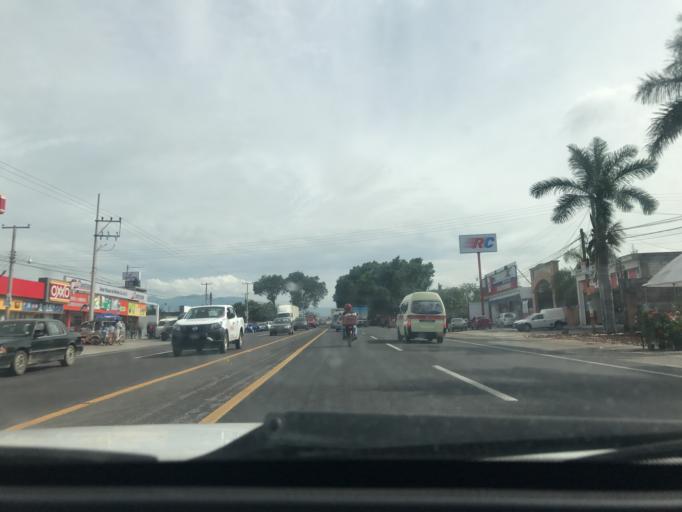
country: MX
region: Morelos
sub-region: Atlatlahucan
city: Colonia San Francisco
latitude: 18.8813
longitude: -98.9194
